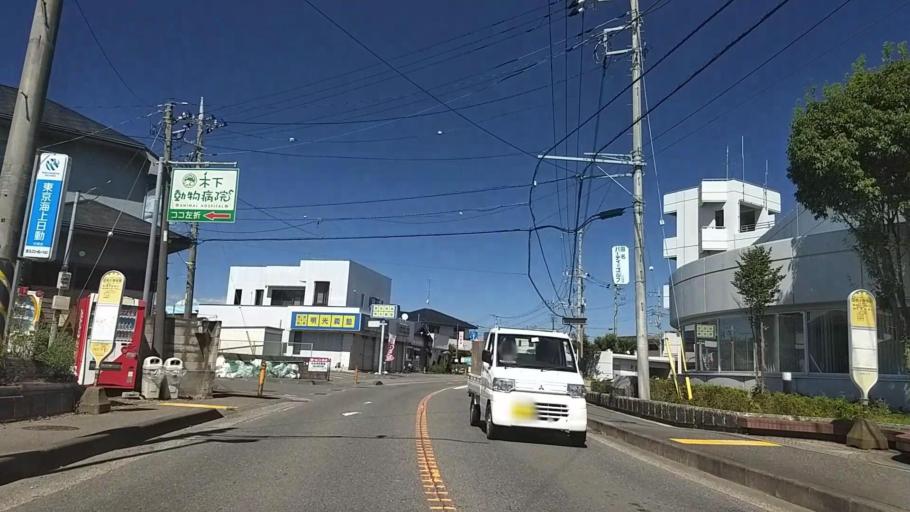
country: JP
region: Kanagawa
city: Zama
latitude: 35.5490
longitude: 139.3357
